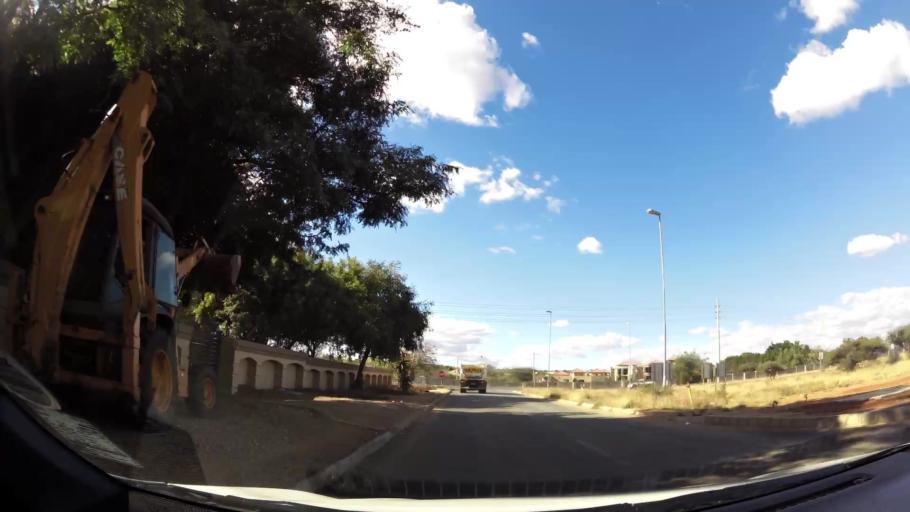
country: ZA
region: Limpopo
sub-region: Capricorn District Municipality
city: Polokwane
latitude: -23.8782
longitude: 29.4930
